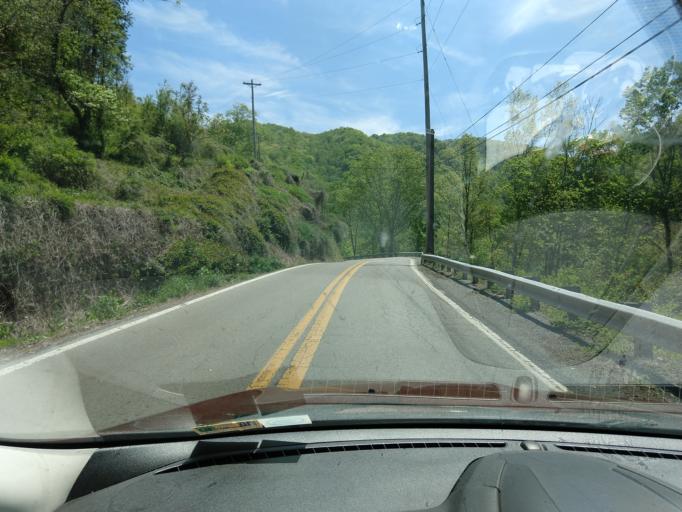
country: US
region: West Virginia
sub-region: McDowell County
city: Welch
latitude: 37.3053
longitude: -81.6926
